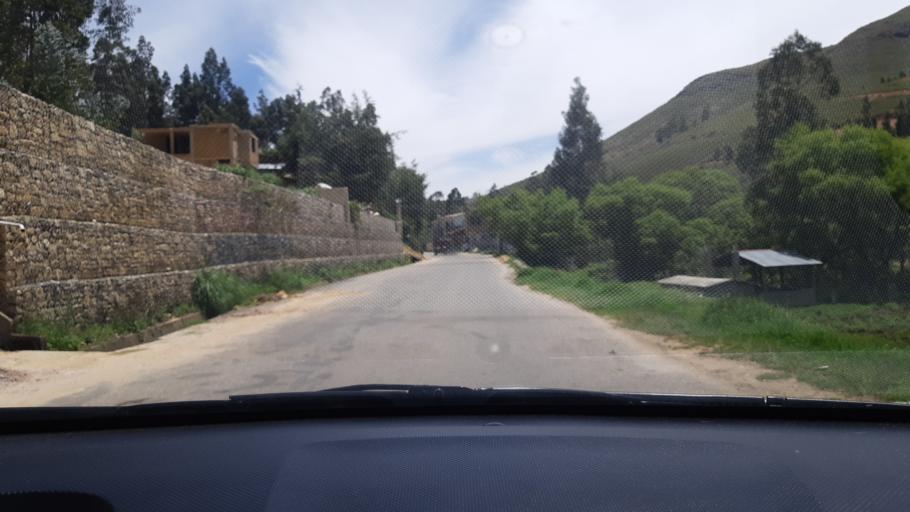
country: PE
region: Cajamarca
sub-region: Provincia de Cajamarca
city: Llacanora
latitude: -7.1854
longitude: -78.4418
